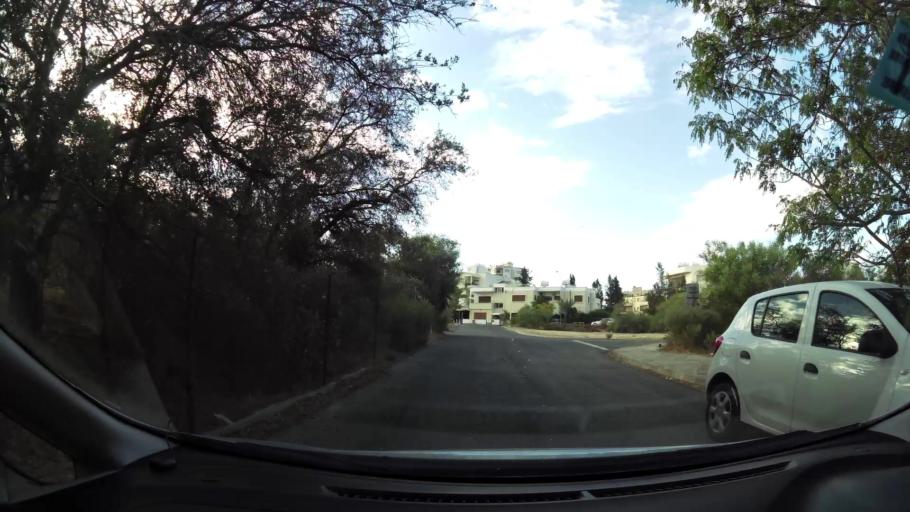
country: CY
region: Lefkosia
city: Nicosia
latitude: 35.1496
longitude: 33.3579
